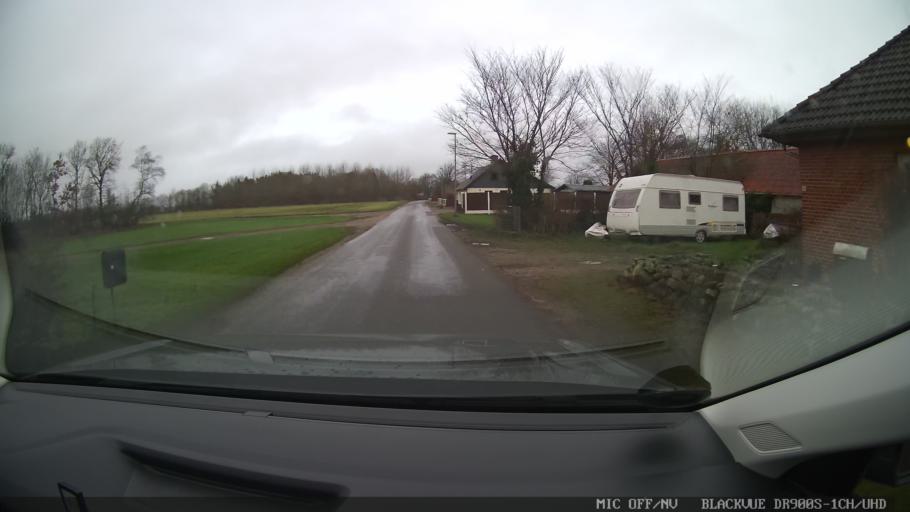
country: DK
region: Central Jutland
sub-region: Viborg Kommune
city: Karup
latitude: 56.3204
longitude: 9.2564
